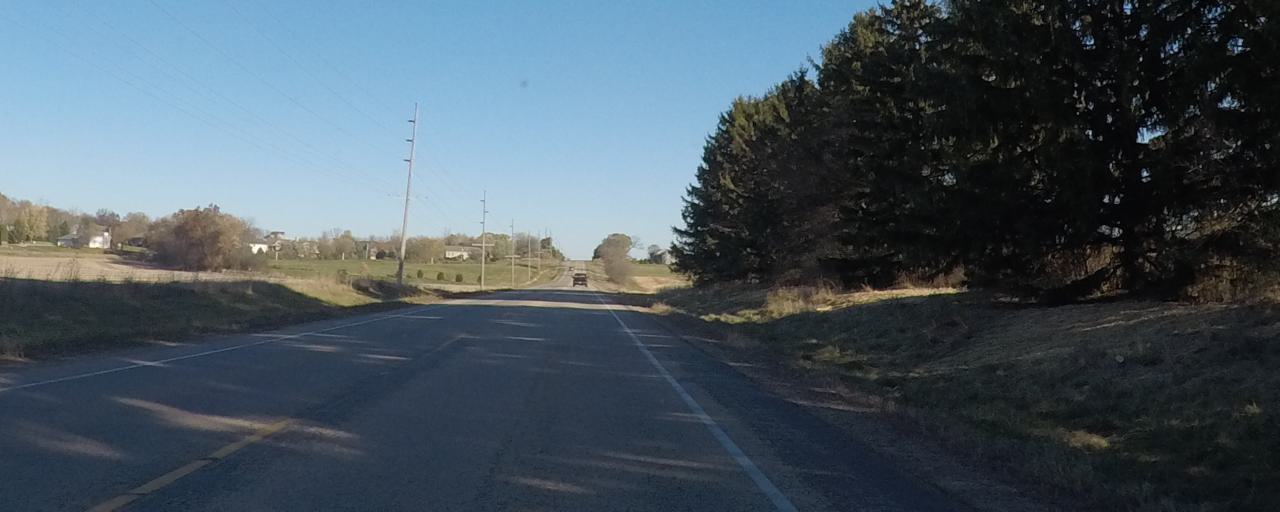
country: US
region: Wisconsin
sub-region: Dane County
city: Cottage Grove
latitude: 43.0440
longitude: -89.1999
